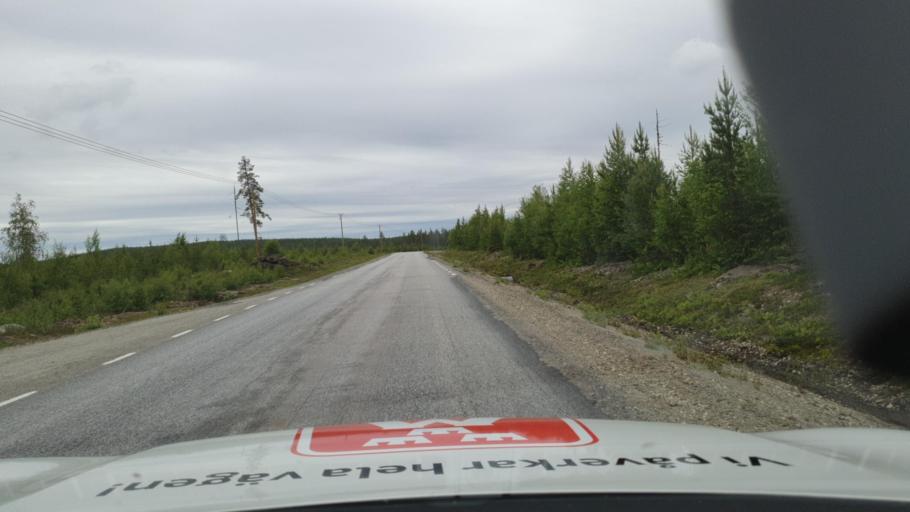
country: SE
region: Vaesterbotten
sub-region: Lycksele Kommun
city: Lycksele
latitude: 64.1181
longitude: 18.3612
